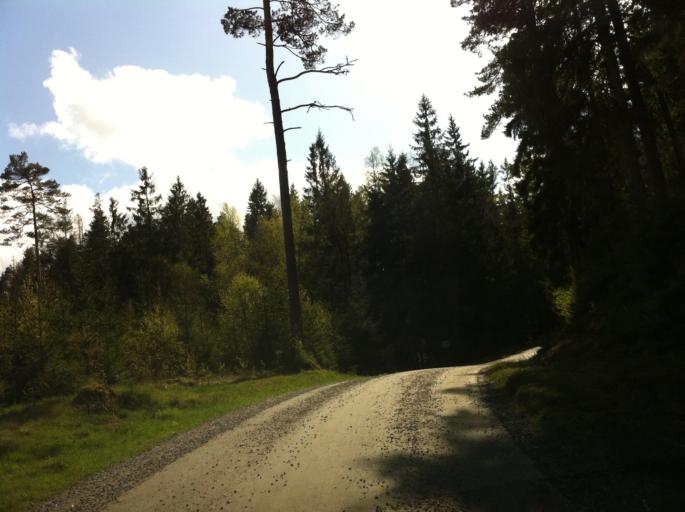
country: SE
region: Vaestra Goetaland
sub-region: Bollebygds Kommun
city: Bollebygd
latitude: 57.7738
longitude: 12.5981
